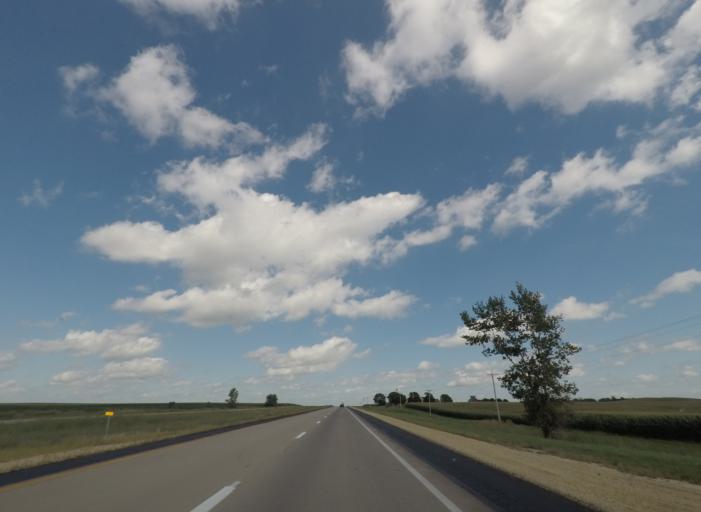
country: US
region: Iowa
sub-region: Jones County
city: Monticello
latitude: 42.2818
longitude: -91.1251
